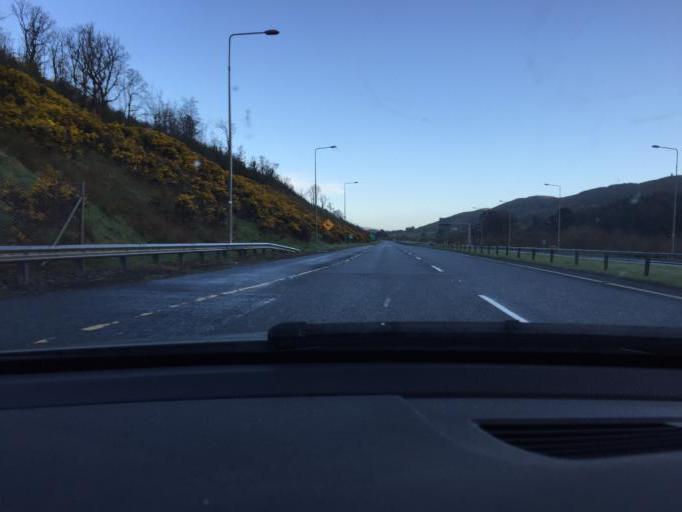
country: IE
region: Leinster
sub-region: Lu
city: Dundalk
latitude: 54.0722
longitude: -6.3514
